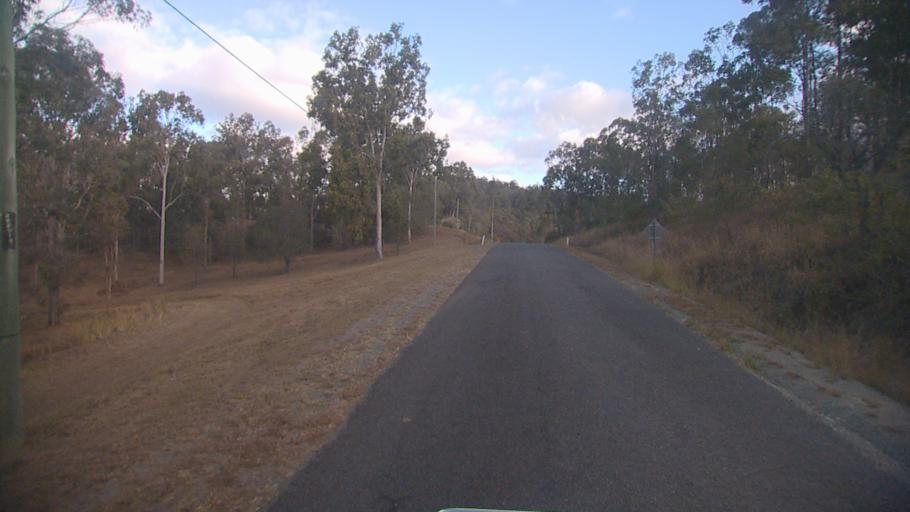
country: AU
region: Queensland
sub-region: Logan
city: Cedar Vale
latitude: -27.9028
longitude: 153.0737
